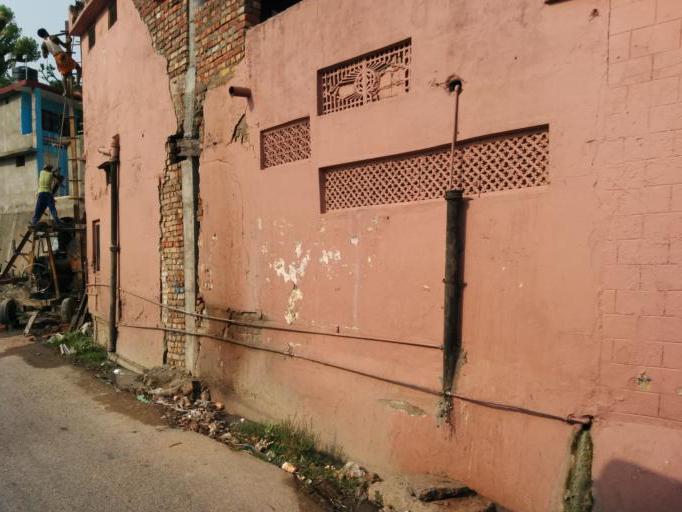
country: IN
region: Punjab
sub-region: Gurdaspur
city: Dharkalan
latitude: 32.2982
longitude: 75.8805
